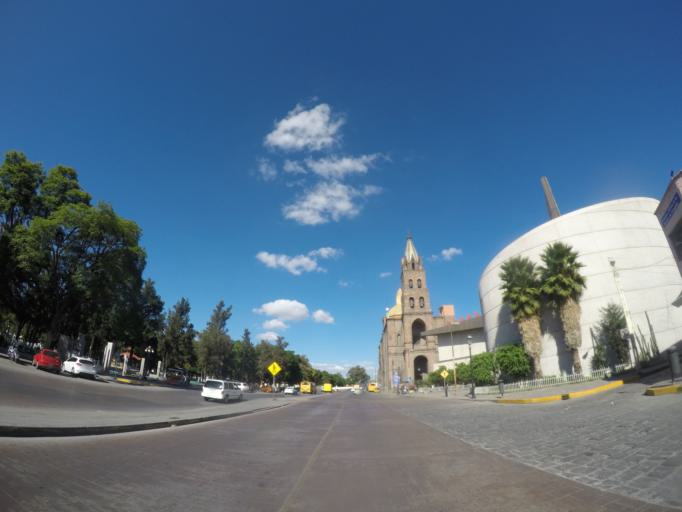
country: MX
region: San Luis Potosi
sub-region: San Luis Potosi
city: San Luis Potosi
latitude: 22.1508
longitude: -100.9711
